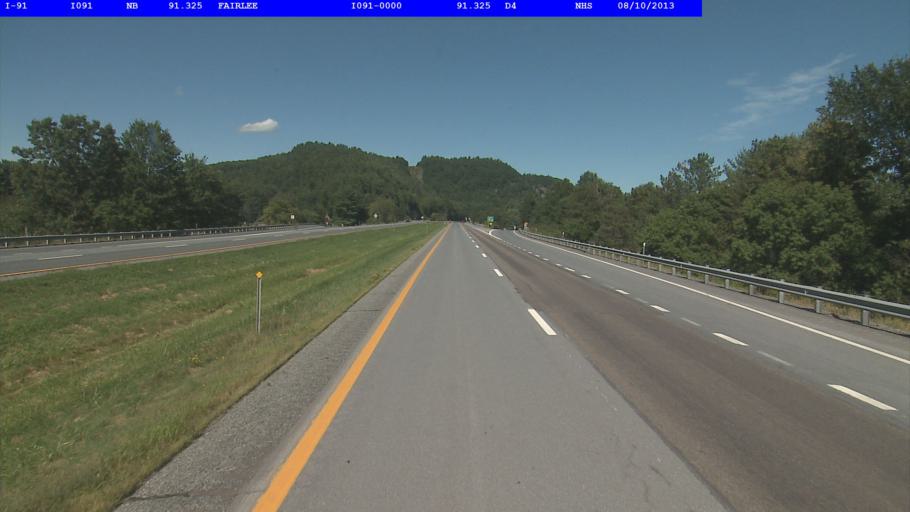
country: US
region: New Hampshire
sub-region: Grafton County
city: Orford
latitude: 43.9030
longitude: -72.1545
